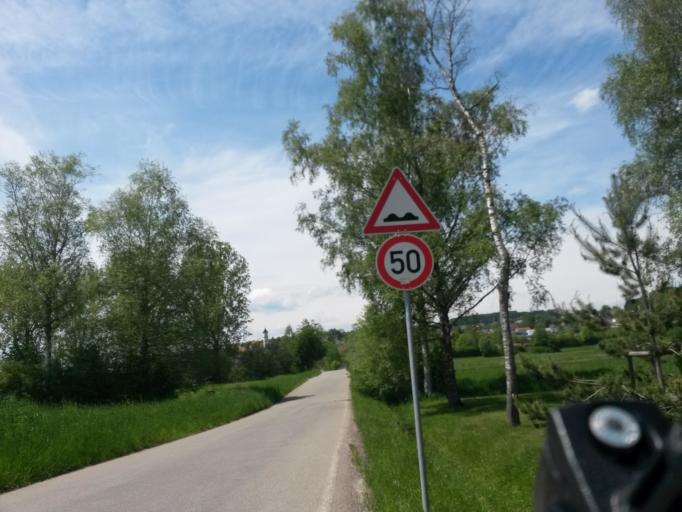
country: DE
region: Baden-Wuerttemberg
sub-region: Tuebingen Region
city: Aulendorf
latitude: 47.9538
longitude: 9.6504
